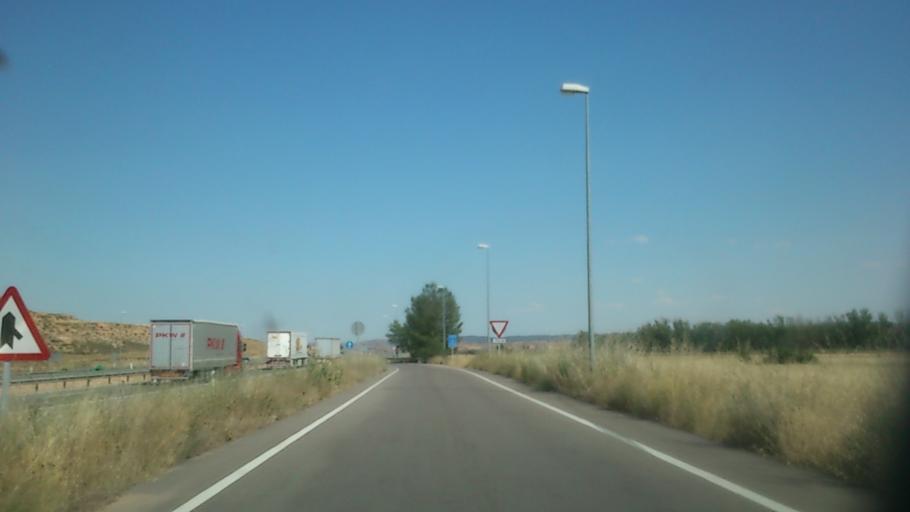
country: ES
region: Aragon
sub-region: Provincia de Zaragoza
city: Cetina
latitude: 41.3107
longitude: -1.9990
